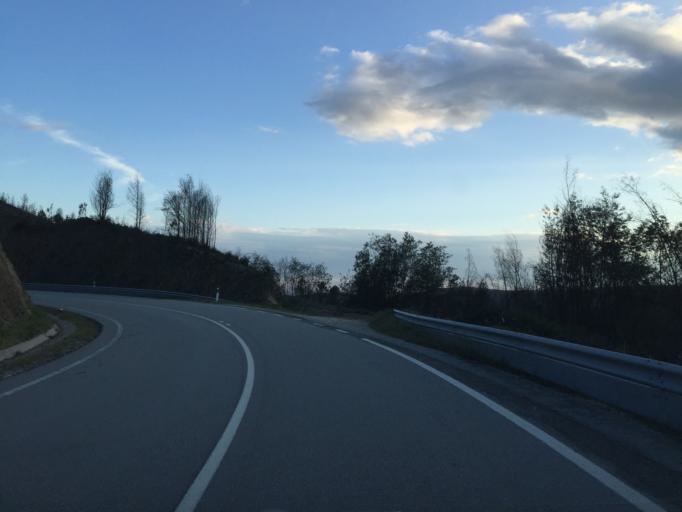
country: PT
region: Coimbra
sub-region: Pampilhosa da Serra
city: Pampilhosa da Serra
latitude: 40.0983
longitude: -7.9876
